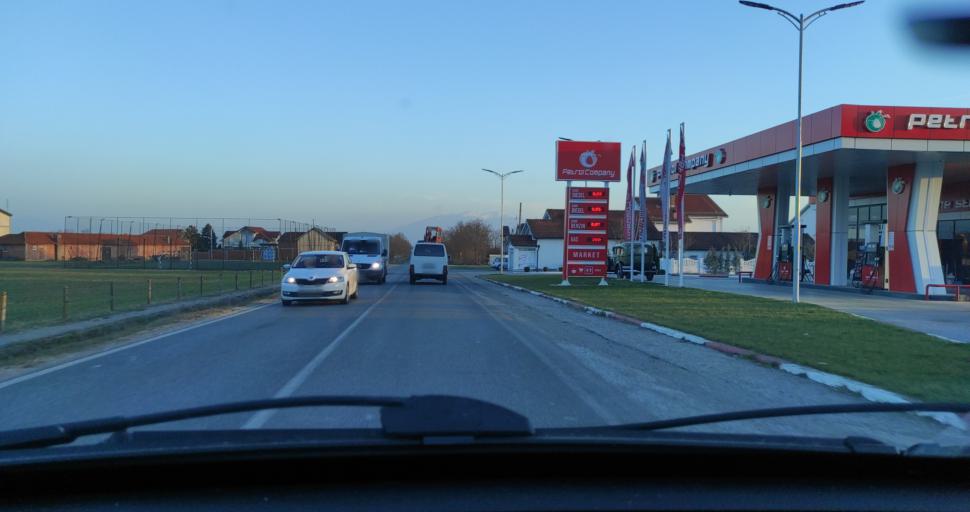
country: XK
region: Gjakova
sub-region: Komuna e Decanit
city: Gllogjan
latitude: 42.4442
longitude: 20.3650
